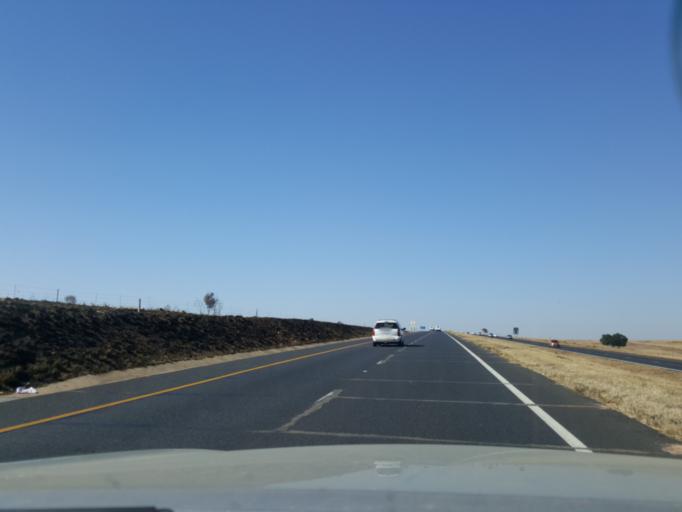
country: ZA
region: Mpumalanga
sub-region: Nkangala District Municipality
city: Witbank
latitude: -25.8776
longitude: 29.3294
